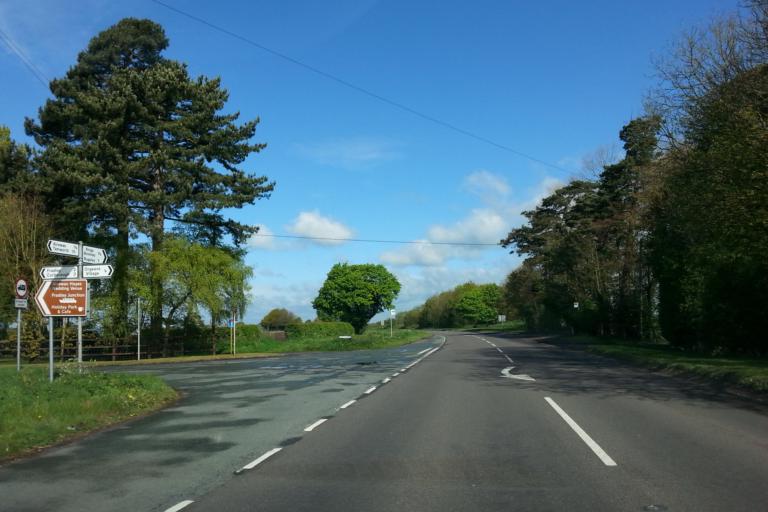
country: GB
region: England
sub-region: Staffordshire
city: Alrewas
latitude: 52.7395
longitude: -1.7829
